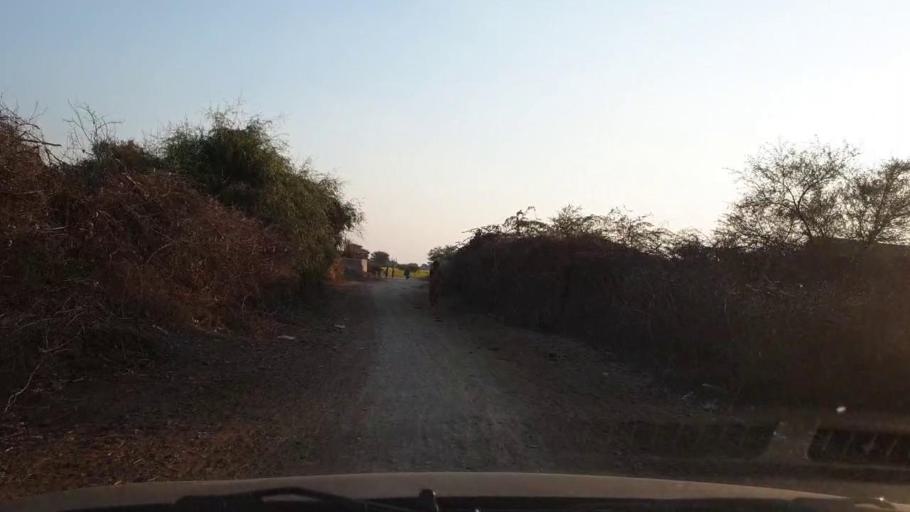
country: PK
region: Sindh
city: Jhol
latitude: 25.9172
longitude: 68.9336
